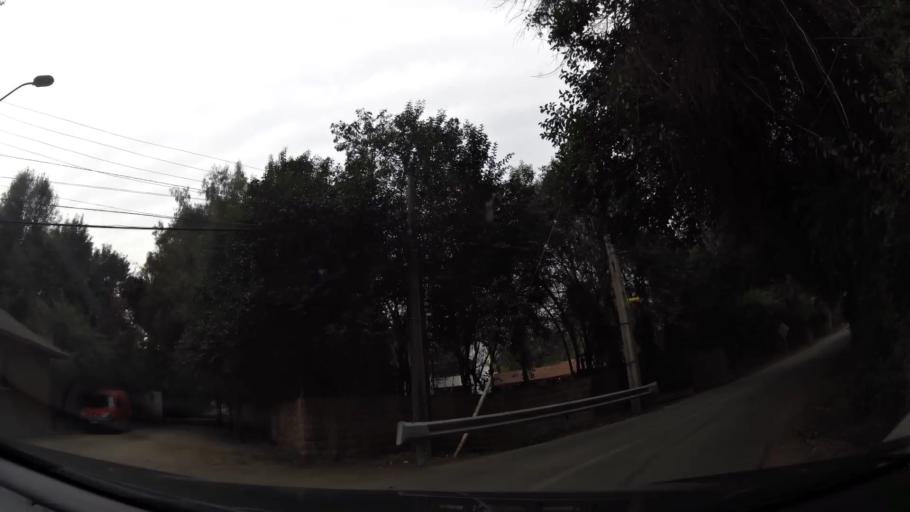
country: CL
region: Santiago Metropolitan
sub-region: Provincia de Chacabuco
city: Chicureo Abajo
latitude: -33.2683
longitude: -70.7103
